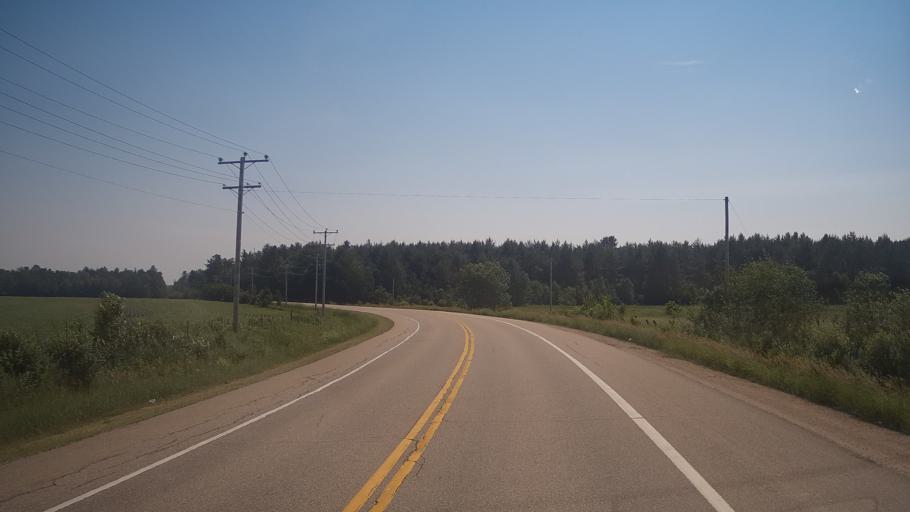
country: CA
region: Ontario
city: Pembroke
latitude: 45.8485
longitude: -77.0128
